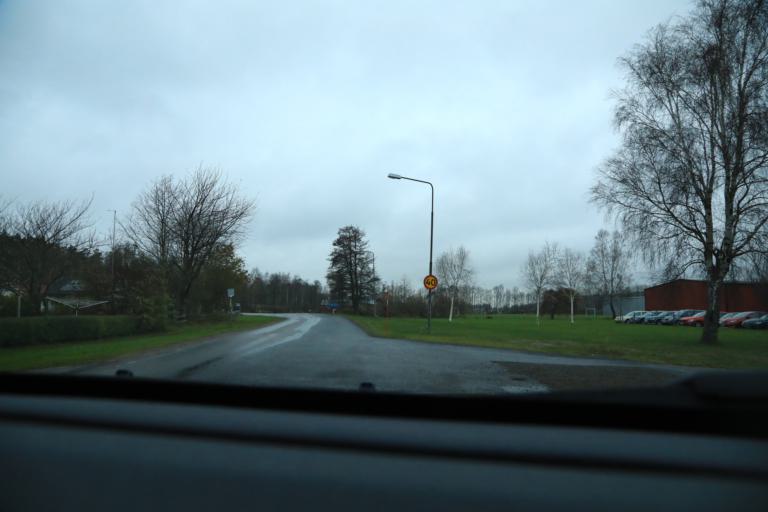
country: SE
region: Halland
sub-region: Varbergs Kommun
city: Varberg
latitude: 57.1752
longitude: 12.2244
